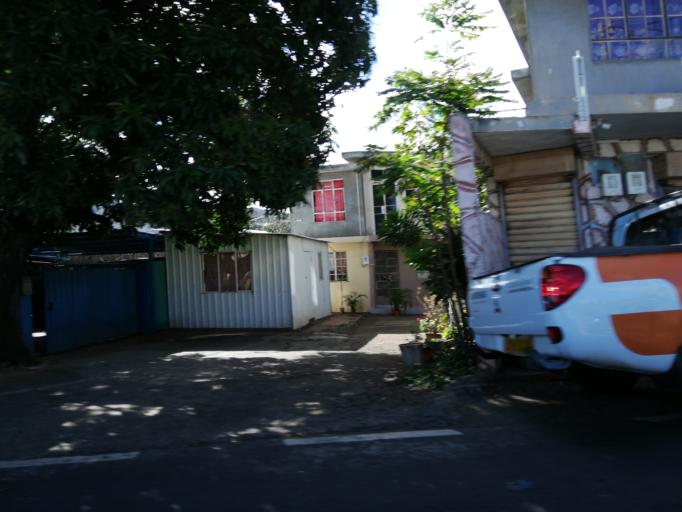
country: MU
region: Moka
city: Pailles
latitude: -20.1888
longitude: 57.4782
